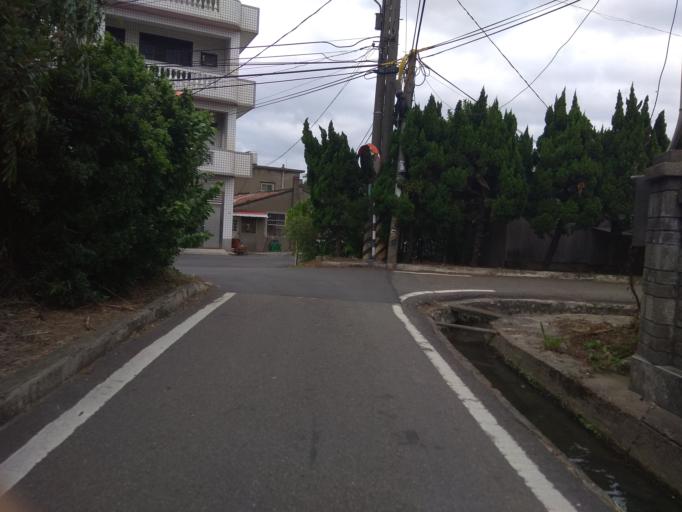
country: TW
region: Taiwan
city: Taoyuan City
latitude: 25.0532
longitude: 121.2183
